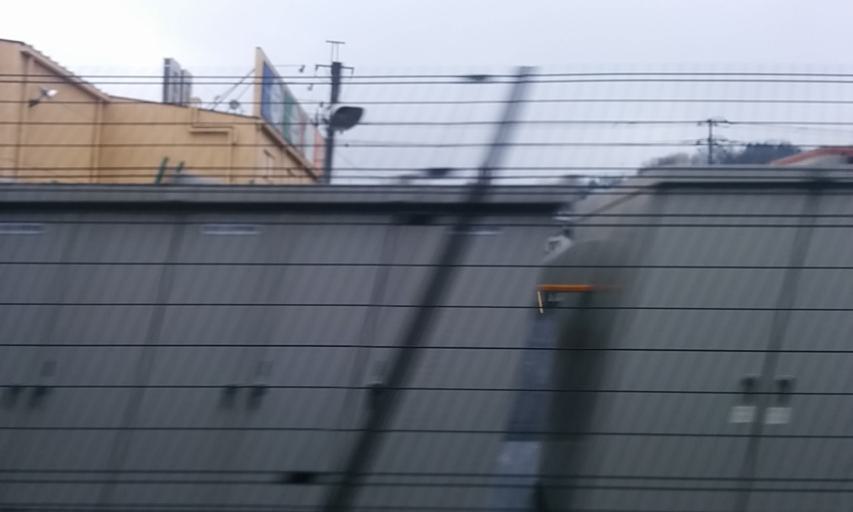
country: JP
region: Tokyo
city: Hino
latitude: 35.6596
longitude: 139.4223
